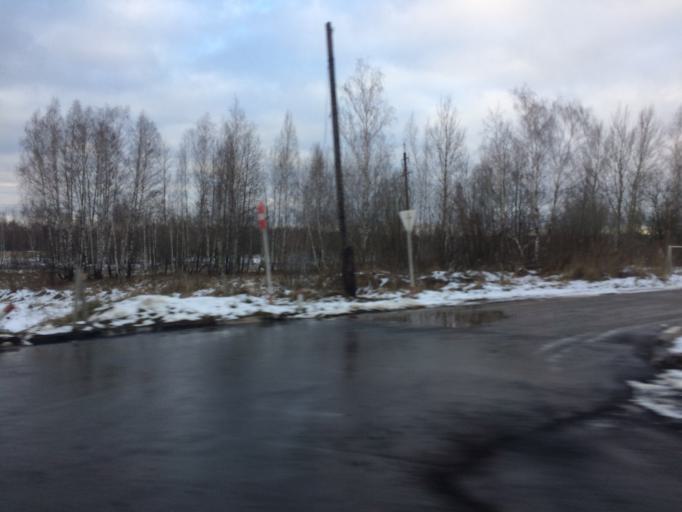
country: RU
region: Tula
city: Ageyevo
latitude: 54.1289
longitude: 36.4615
